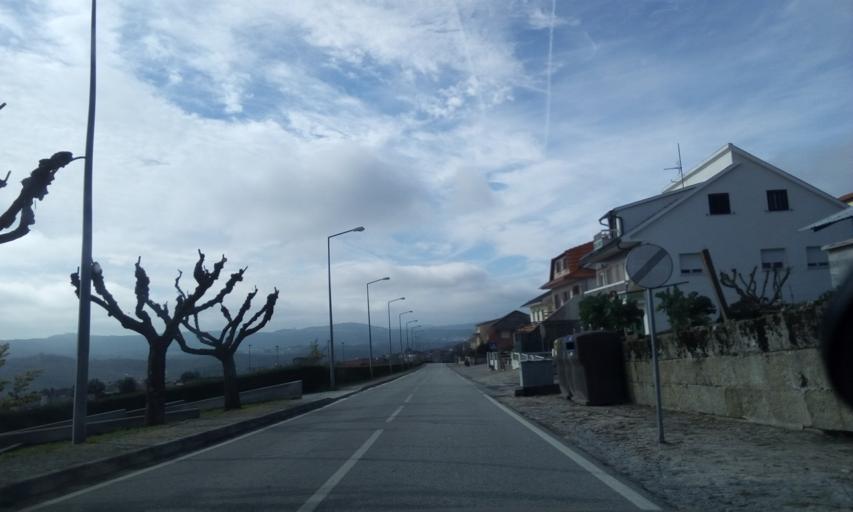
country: PT
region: Guarda
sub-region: Aguiar da Beira
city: Aguiar da Beira
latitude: 40.7391
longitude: -7.5548
